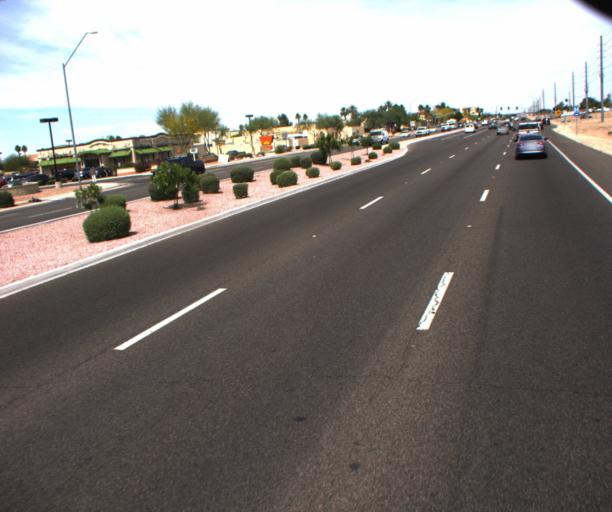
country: US
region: Arizona
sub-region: Maricopa County
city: Sun City West
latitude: 33.6553
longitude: -112.3714
